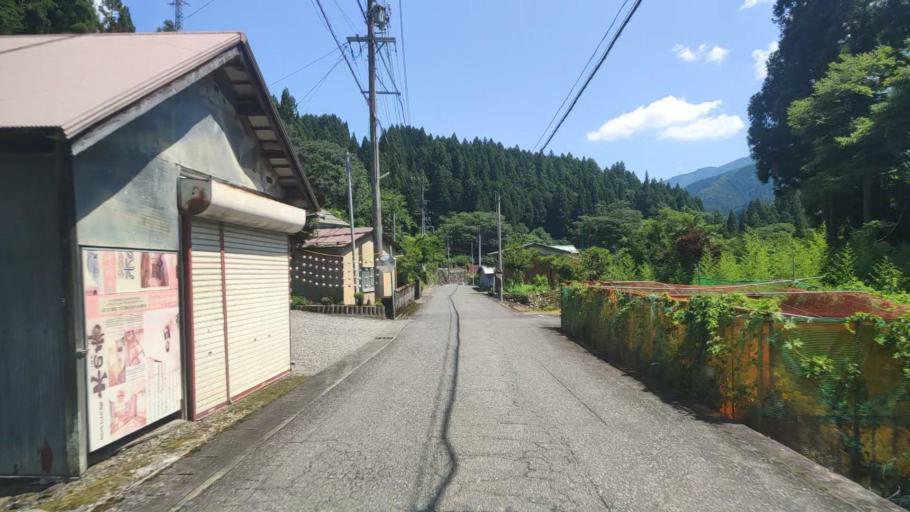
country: JP
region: Gifu
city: Godo
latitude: 35.6708
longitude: 136.5769
